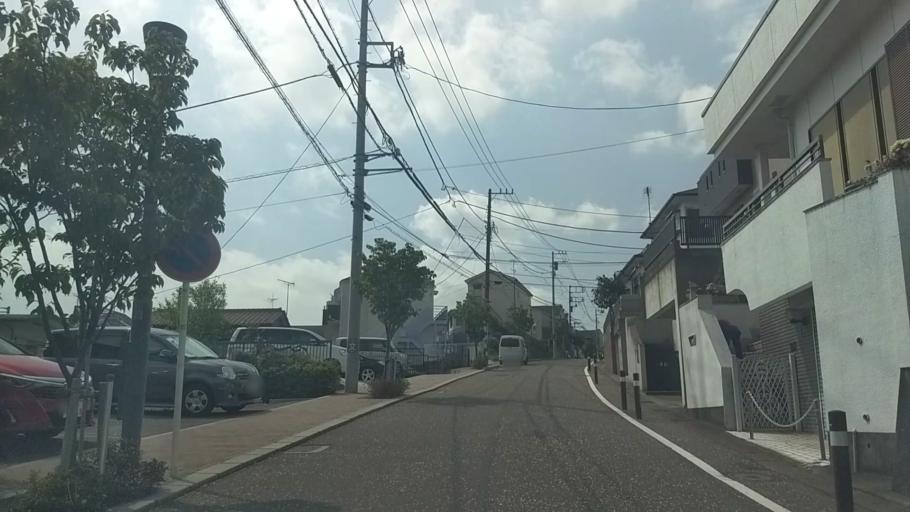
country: JP
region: Kanagawa
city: Yokohama
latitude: 35.3955
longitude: 139.5922
